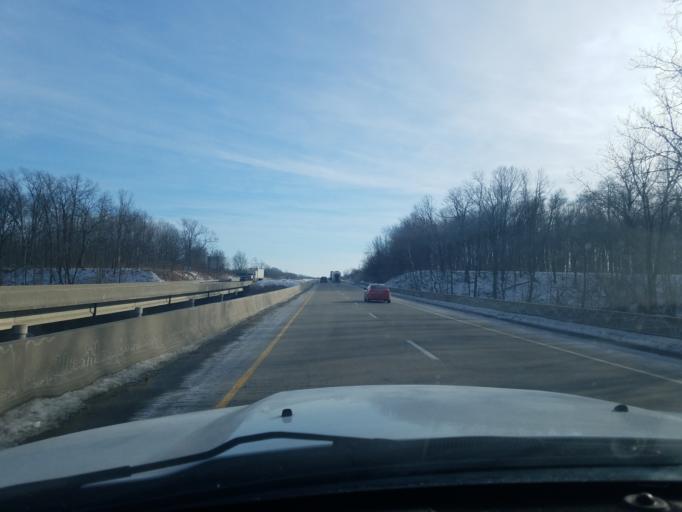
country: US
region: Indiana
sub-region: Grant County
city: Upland
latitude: 40.4556
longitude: -85.5502
